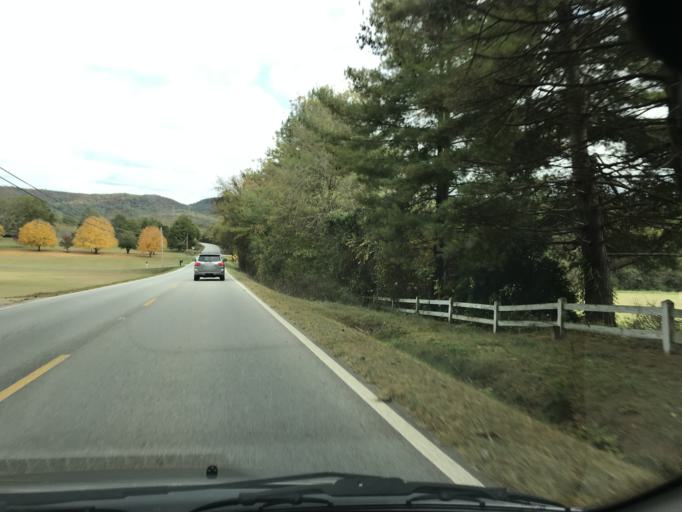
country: US
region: Tennessee
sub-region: Hamilton County
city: Lakesite
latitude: 35.1782
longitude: -85.0448
